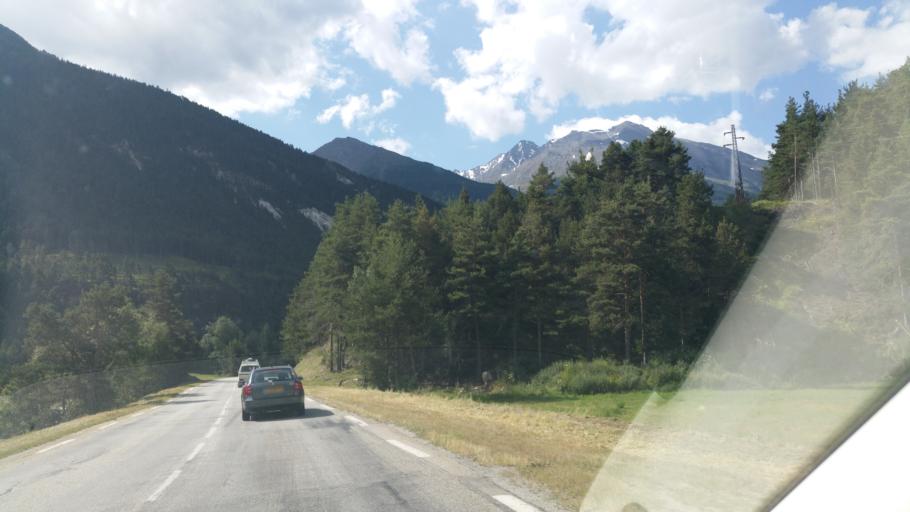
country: FR
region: Rhone-Alpes
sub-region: Departement de la Savoie
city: Modane
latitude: 45.2425
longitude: 6.7923
